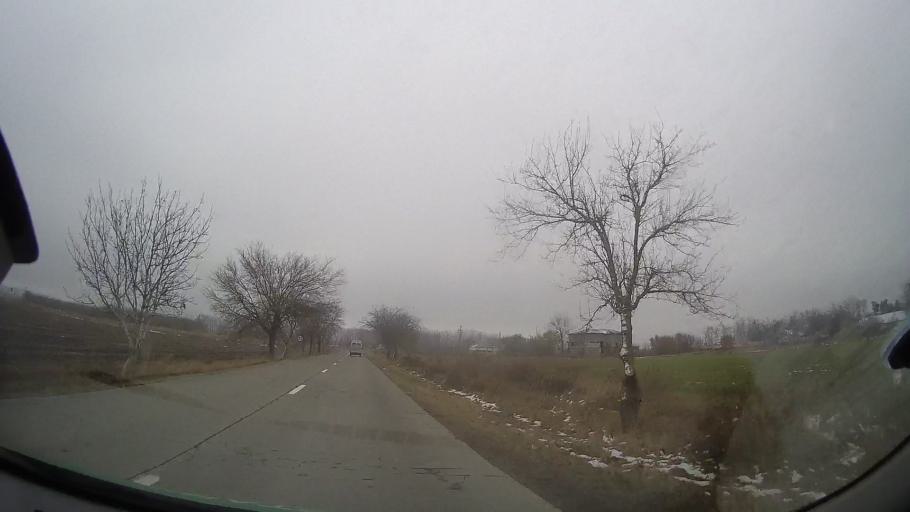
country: RO
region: Vaslui
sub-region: Municipiul Barlad
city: Barlad
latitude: 46.1981
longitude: 27.6402
